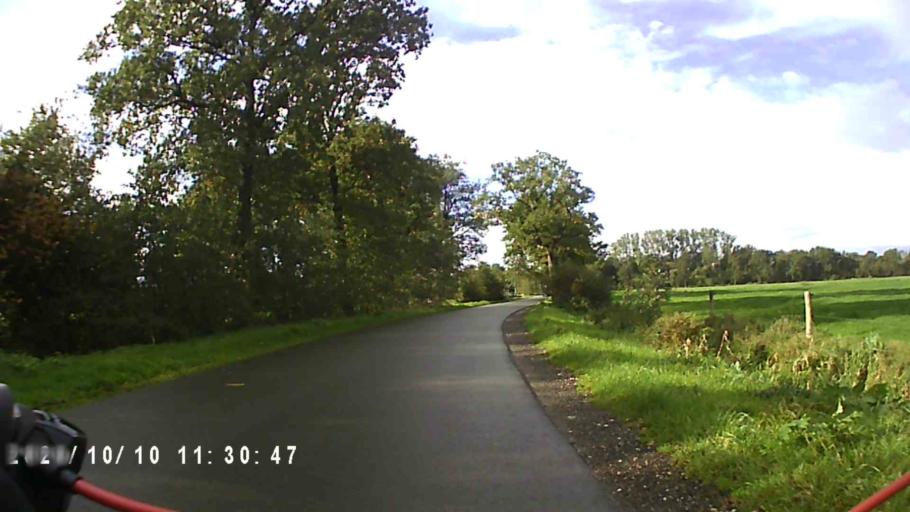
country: NL
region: Friesland
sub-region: Gemeente Smallingerland
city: Drachtstercompagnie
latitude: 53.0853
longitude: 6.1416
